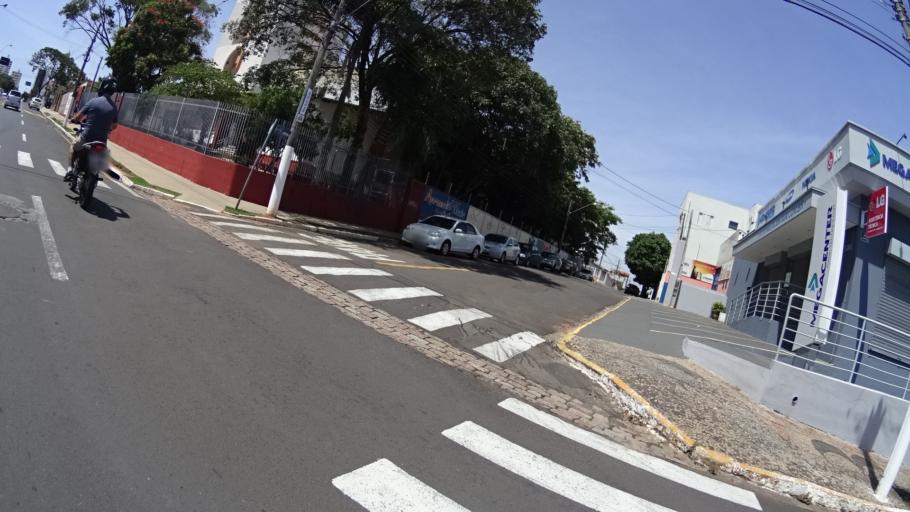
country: BR
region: Sao Paulo
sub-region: Marilia
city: Marilia
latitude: -22.2156
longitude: -49.9543
